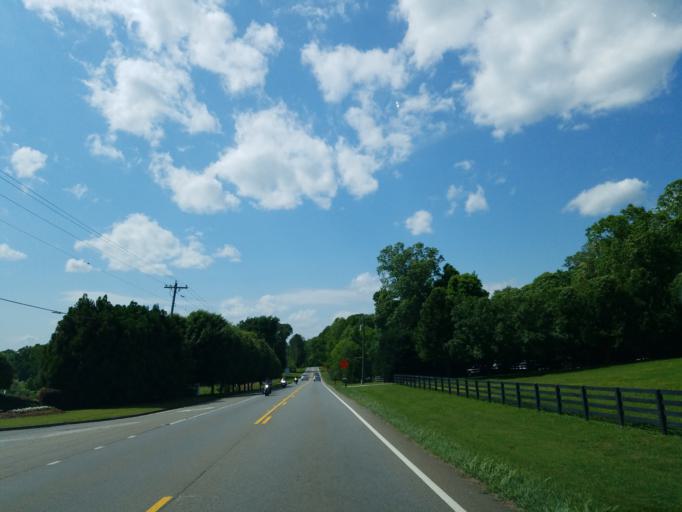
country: US
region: Georgia
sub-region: Cherokee County
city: Ball Ground
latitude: 34.2679
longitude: -84.2911
